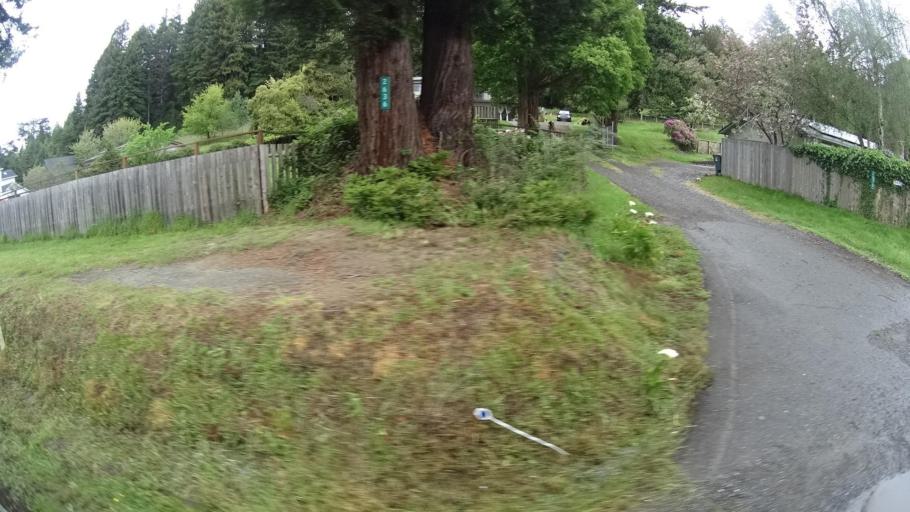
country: US
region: California
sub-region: Humboldt County
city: Bayside
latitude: 40.8404
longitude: -124.0593
